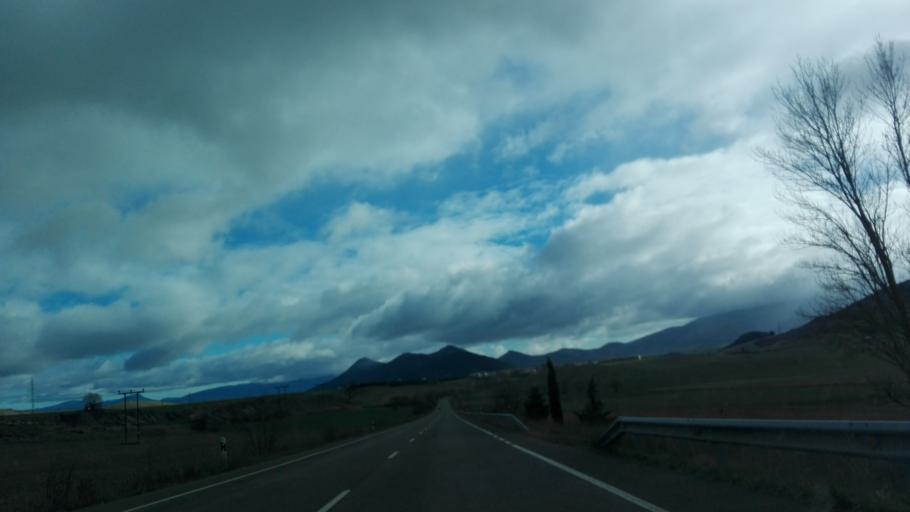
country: ES
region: Navarre
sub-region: Provincia de Navarra
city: Lizoain
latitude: 42.7911
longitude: -1.4739
